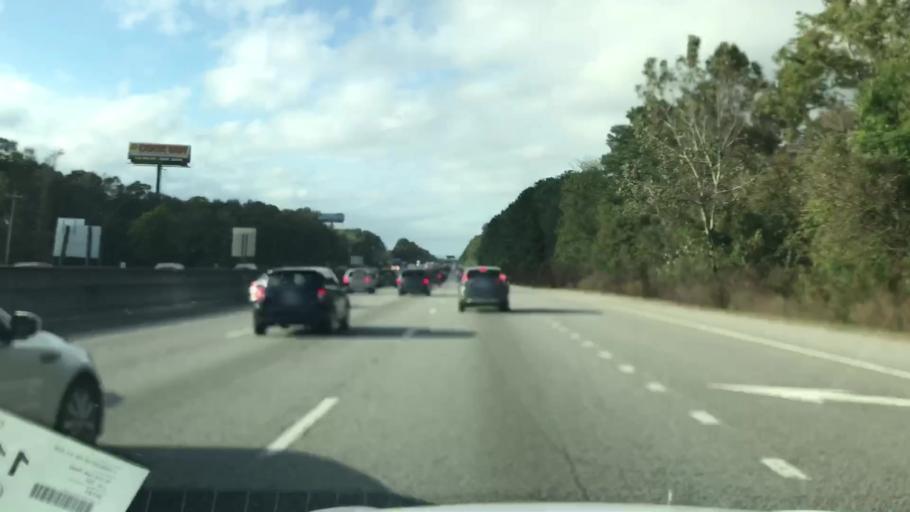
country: US
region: South Carolina
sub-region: Berkeley County
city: Hanahan
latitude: 32.9448
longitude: -80.0541
